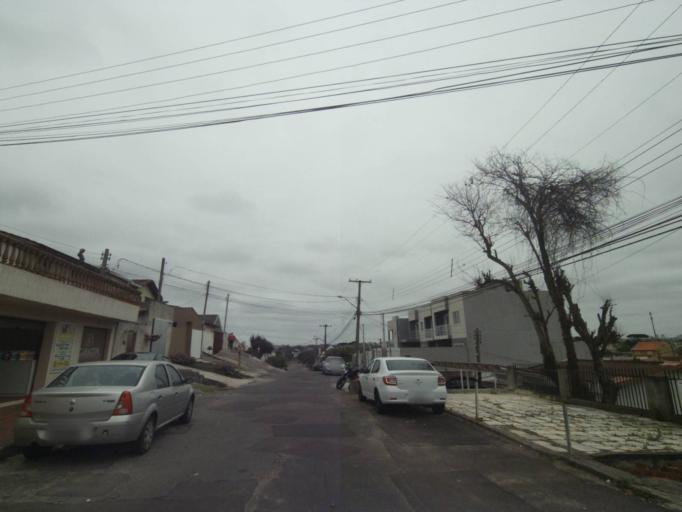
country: BR
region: Parana
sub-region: Pinhais
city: Pinhais
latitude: -25.4774
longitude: -49.2367
